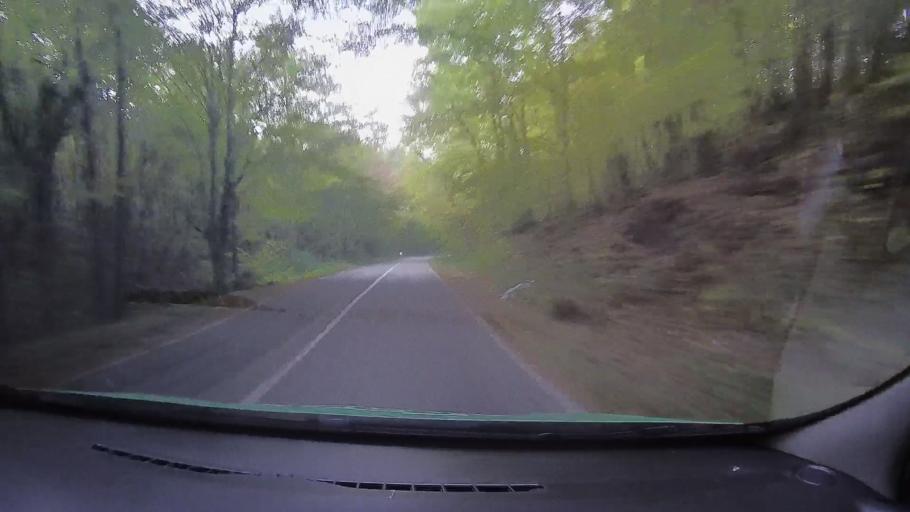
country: RO
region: Timis
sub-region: Comuna Nadrag
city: Nadrag
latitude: 45.6878
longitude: 22.1577
